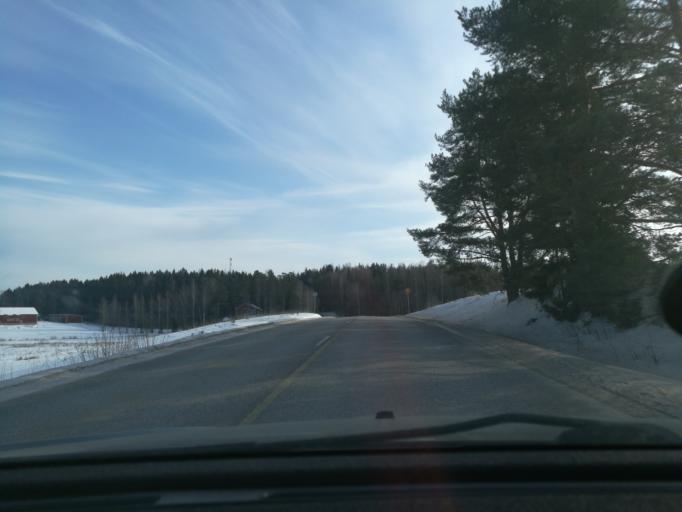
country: FI
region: Uusimaa
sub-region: Helsinki
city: Saukkola
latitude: 60.3910
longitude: 24.0760
